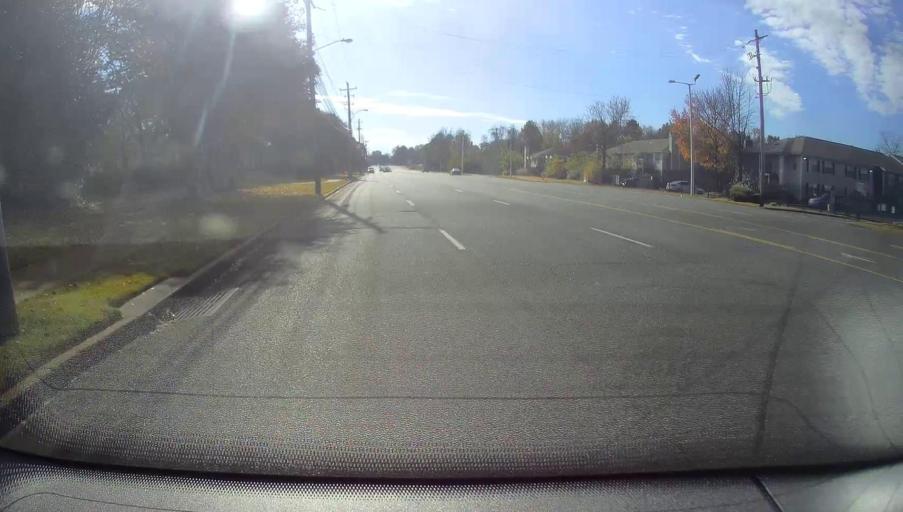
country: US
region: Tennessee
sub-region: Shelby County
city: Germantown
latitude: 35.0632
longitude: -89.8437
